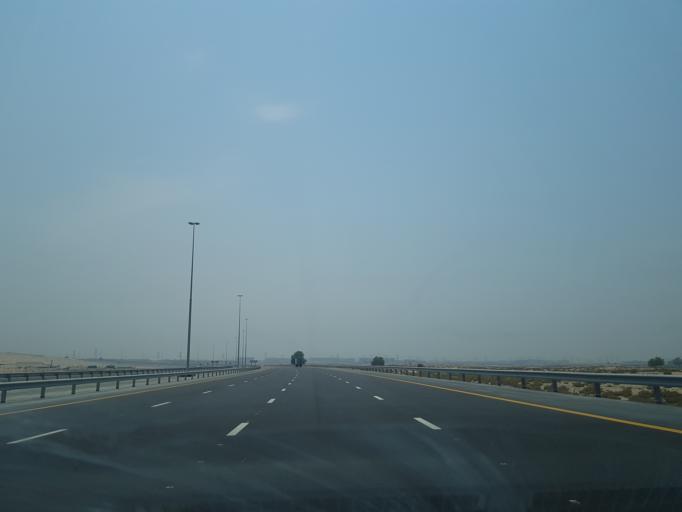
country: AE
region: Dubai
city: Dubai
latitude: 25.0094
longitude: 55.1996
